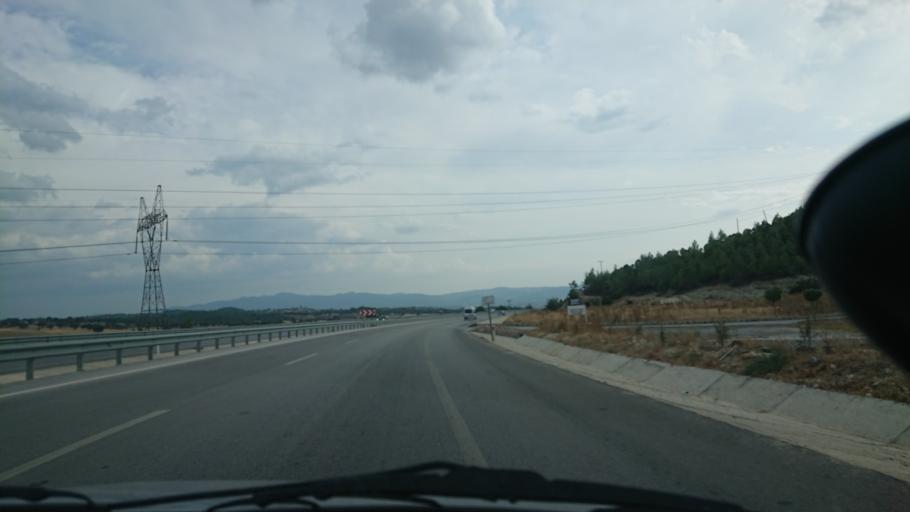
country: TR
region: Kuetahya
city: Gediz
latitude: 39.0284
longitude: 29.4164
